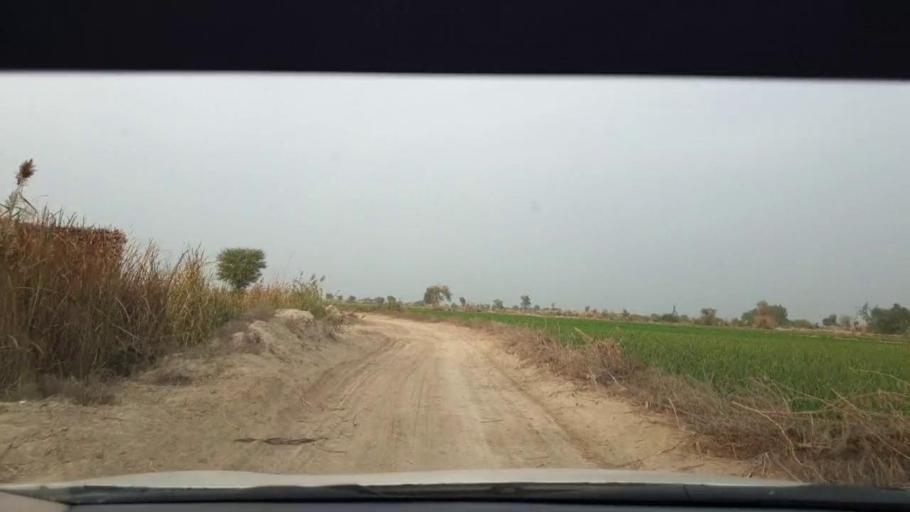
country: PK
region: Sindh
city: Jhol
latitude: 25.9093
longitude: 68.7857
